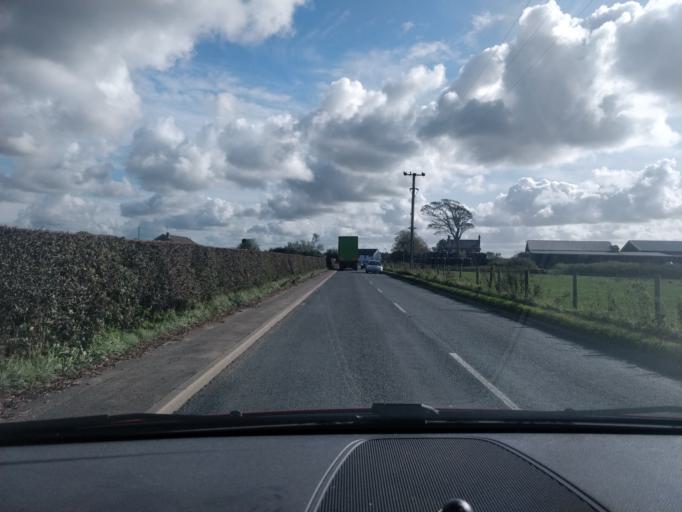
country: GB
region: England
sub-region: Lancashire
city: Ormskirk
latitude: 53.5962
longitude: -2.8961
